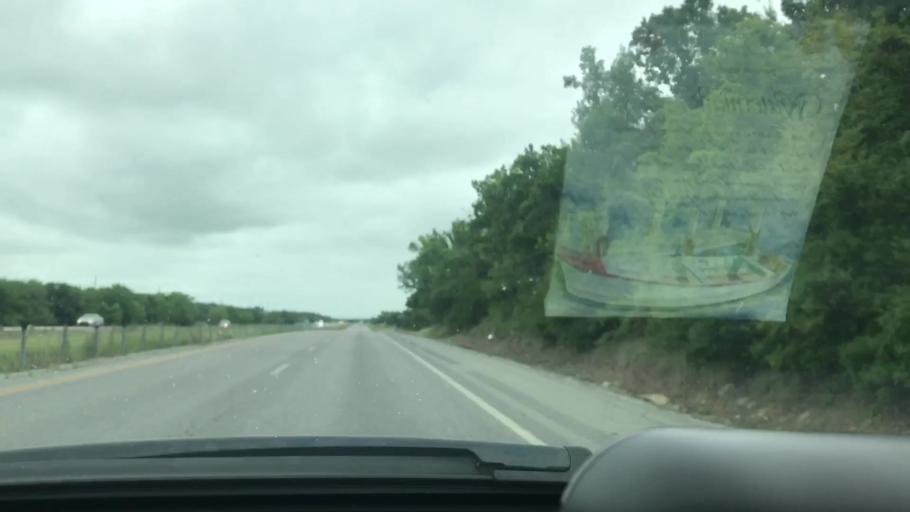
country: US
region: Oklahoma
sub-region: Coal County
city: Coalgate
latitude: 34.6296
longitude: -95.9578
